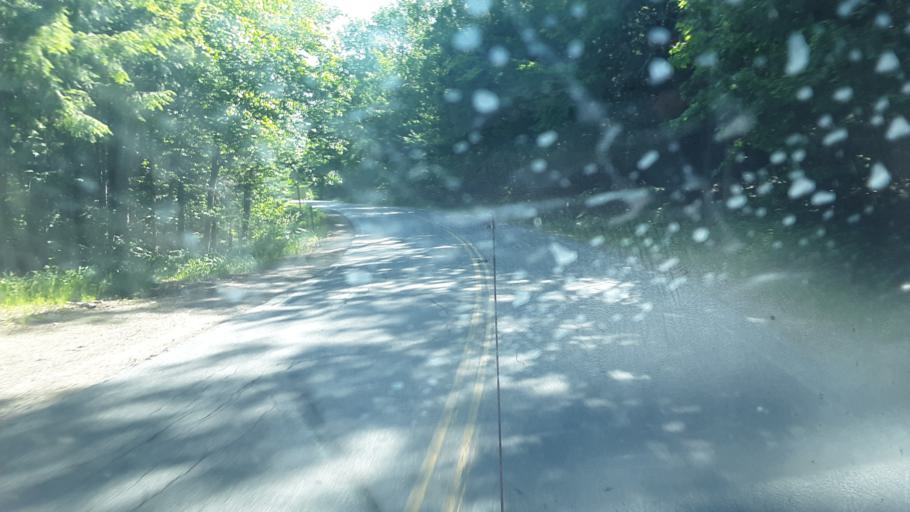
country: US
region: New Hampshire
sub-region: Grafton County
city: North Haverhill
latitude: 44.0978
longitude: -71.8568
